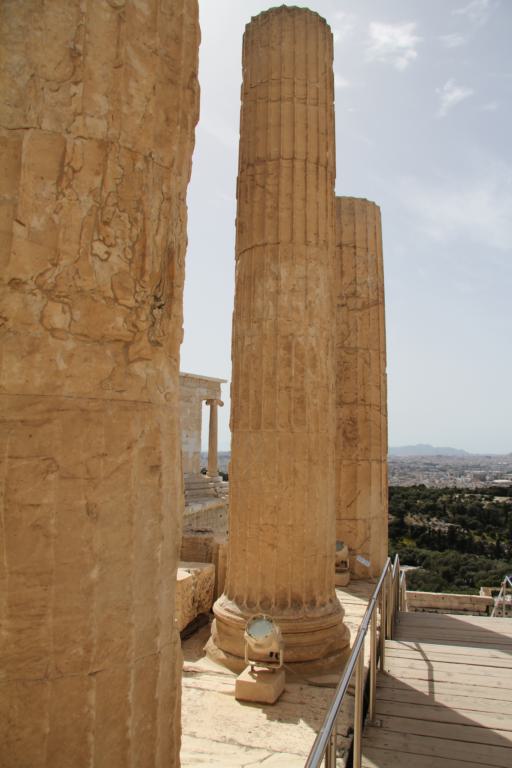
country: GR
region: Attica
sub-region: Nomarchia Athinas
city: Athens
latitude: 37.9717
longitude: 23.7252
